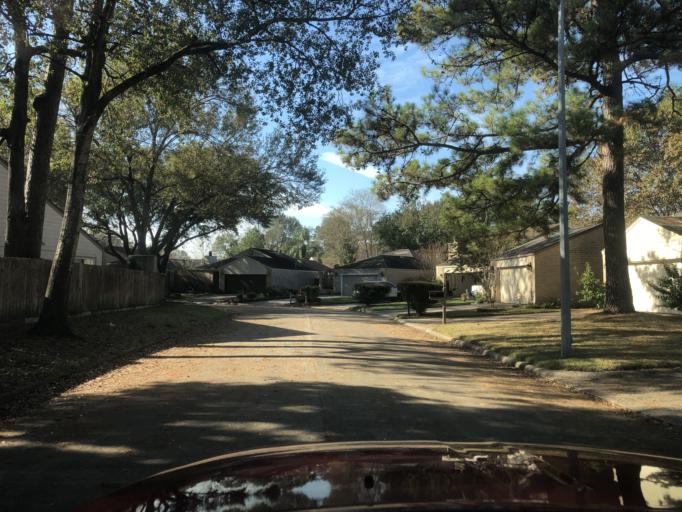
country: US
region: Texas
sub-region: Harris County
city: Spring
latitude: 30.0145
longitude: -95.4598
